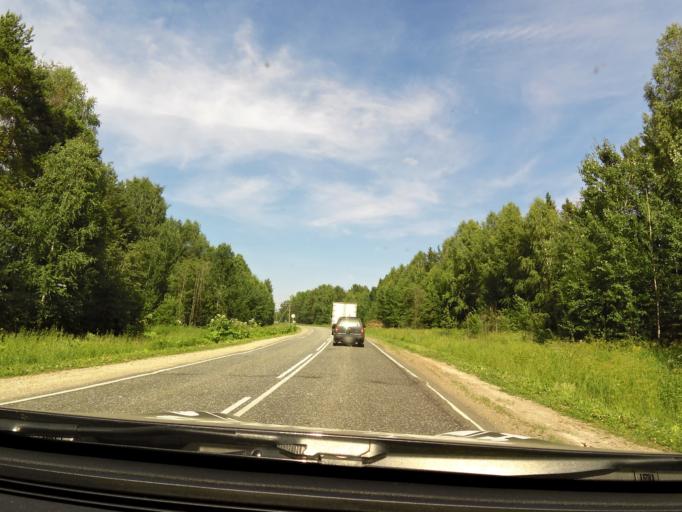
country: RU
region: Kirov
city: Slobodskoy
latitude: 58.7876
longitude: 50.5090
